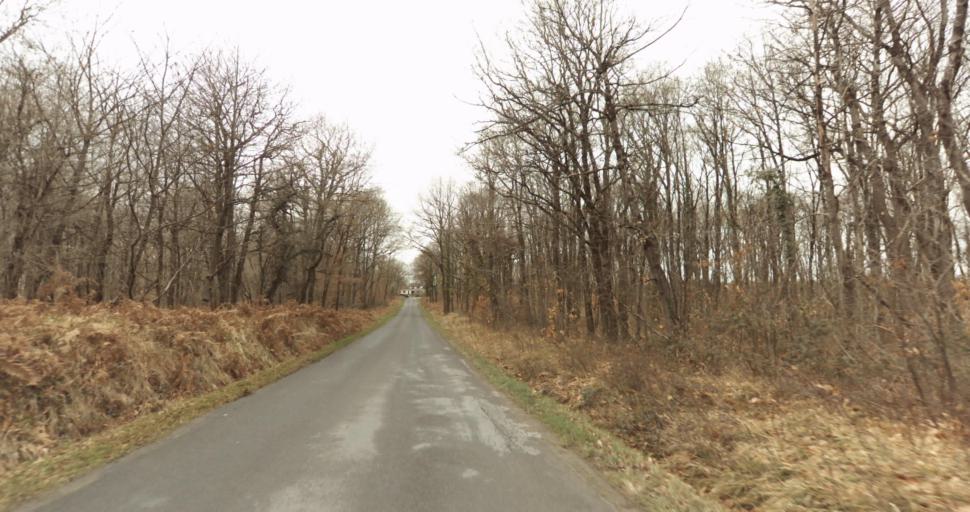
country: FR
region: Pays de la Loire
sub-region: Departement de Maine-et-Loire
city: Distre
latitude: 47.2543
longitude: -0.1205
